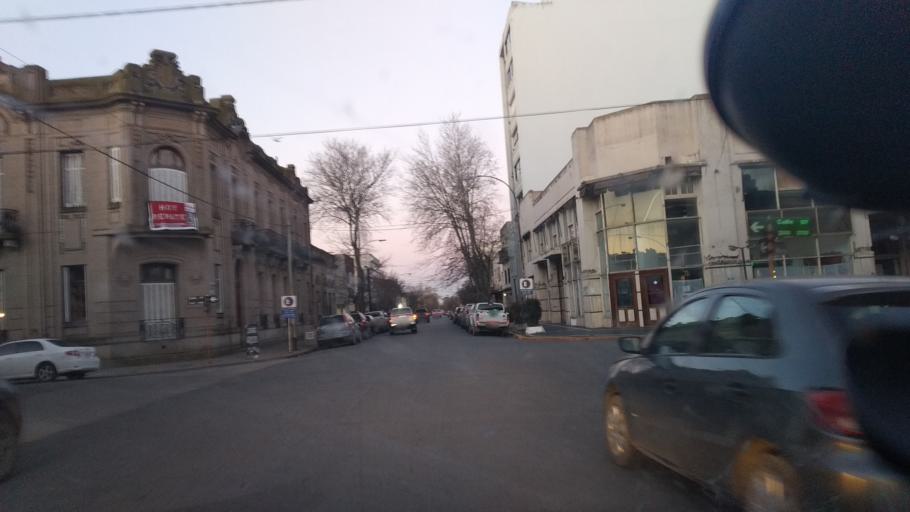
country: AR
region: Buenos Aires
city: Necochea
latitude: -38.5522
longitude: -58.7404
